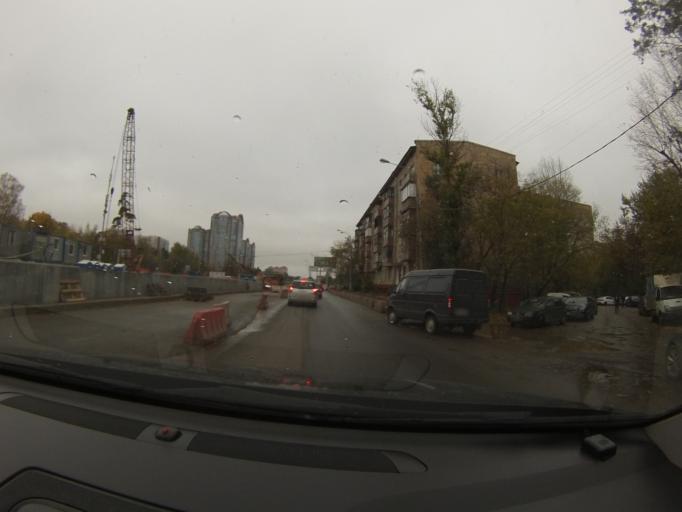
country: RU
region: Moscow
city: Davydkovo
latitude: 55.7199
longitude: 37.4510
